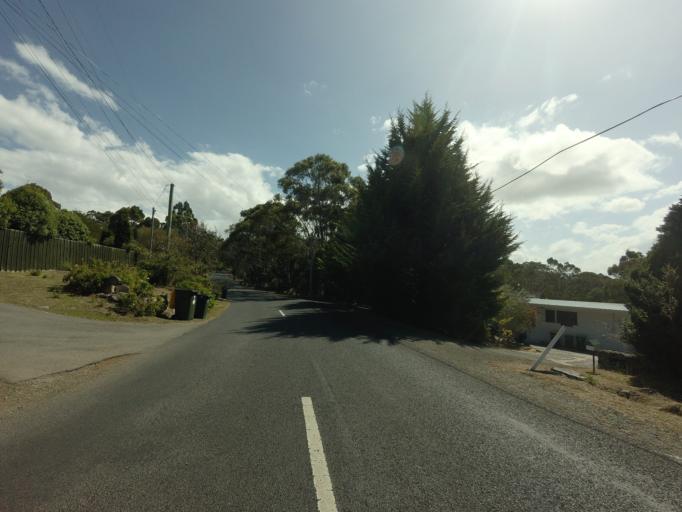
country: AU
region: Tasmania
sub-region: Kingborough
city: Taroona
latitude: -42.9262
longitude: 147.3385
